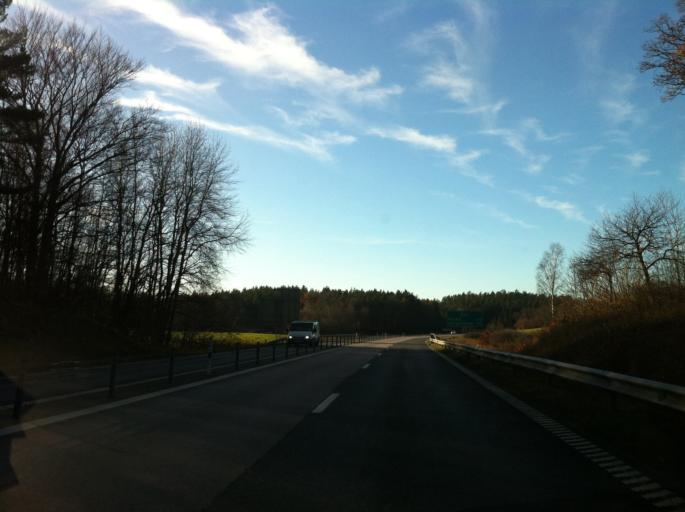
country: SE
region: Blekinge
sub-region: Karlshamns Kommun
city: Karlshamn
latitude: 56.1879
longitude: 14.9168
